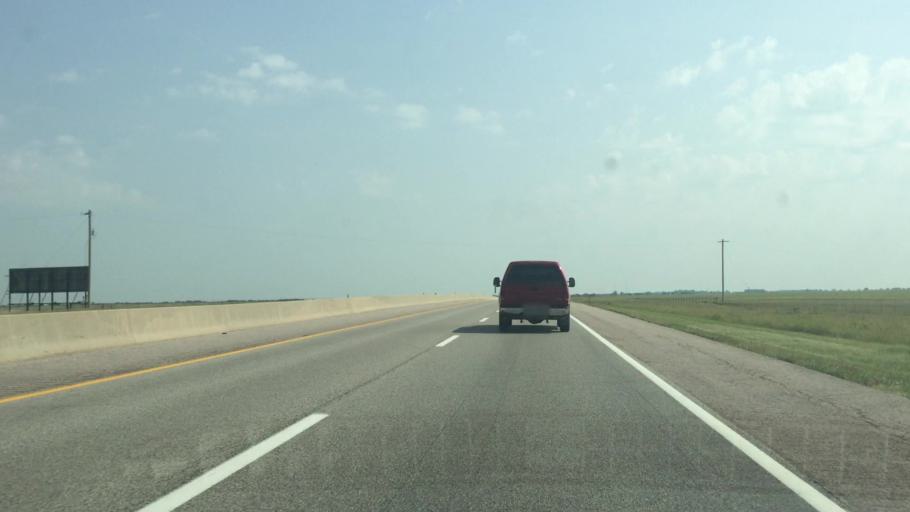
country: US
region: Kansas
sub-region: Butler County
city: El Dorado
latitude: 37.9983
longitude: -96.6924
